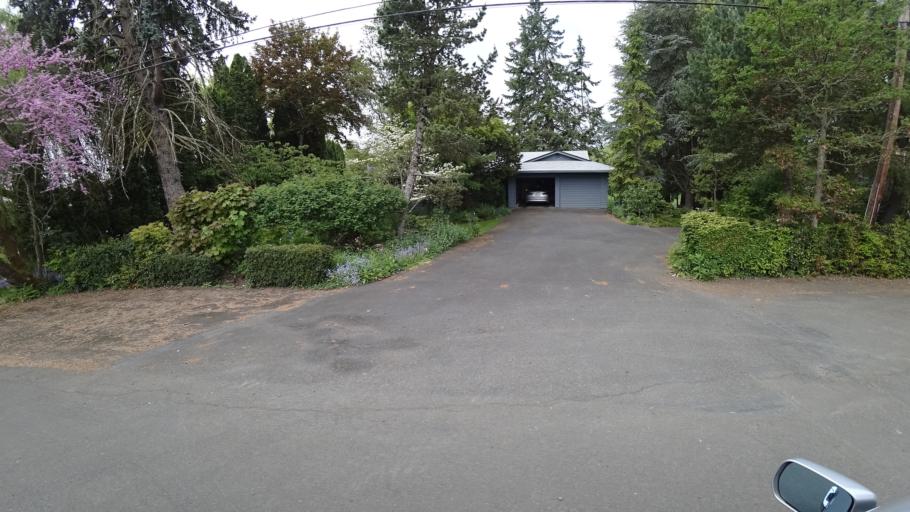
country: US
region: Oregon
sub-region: Washington County
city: Hillsboro
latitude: 45.5281
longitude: -123.0034
